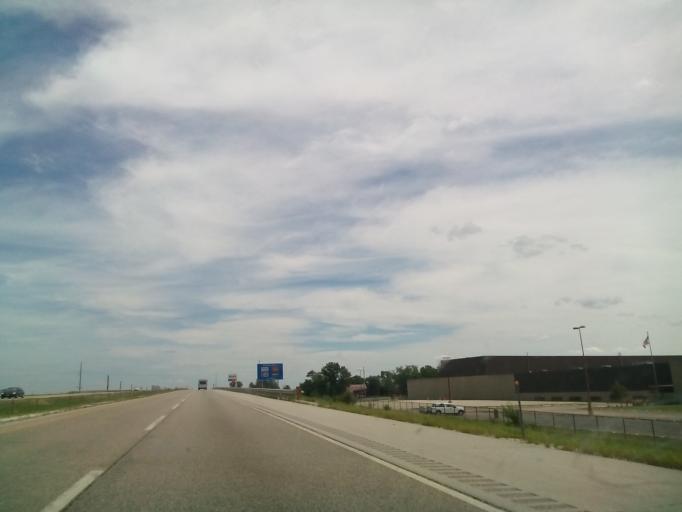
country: US
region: Illinois
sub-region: DeKalb County
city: DeKalb
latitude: 41.9033
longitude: -88.7576
